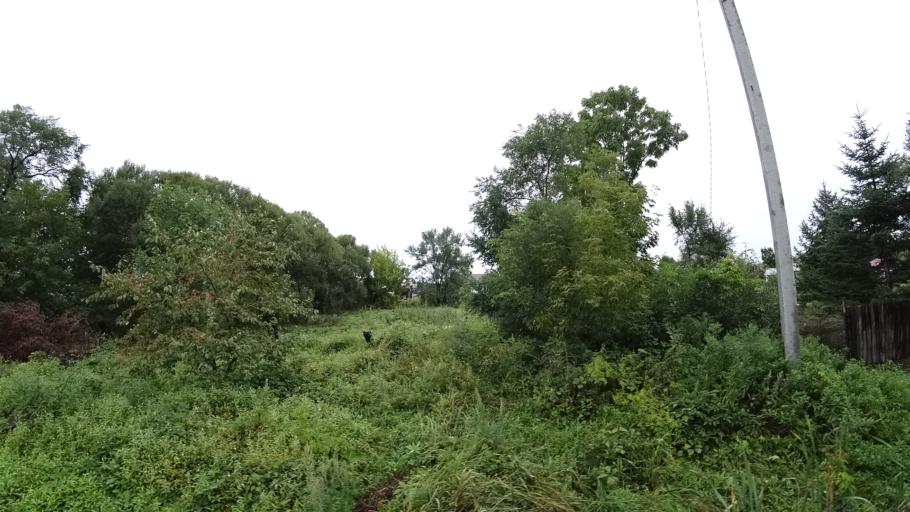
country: RU
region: Primorskiy
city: Monastyrishche
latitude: 44.2083
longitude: 132.4334
